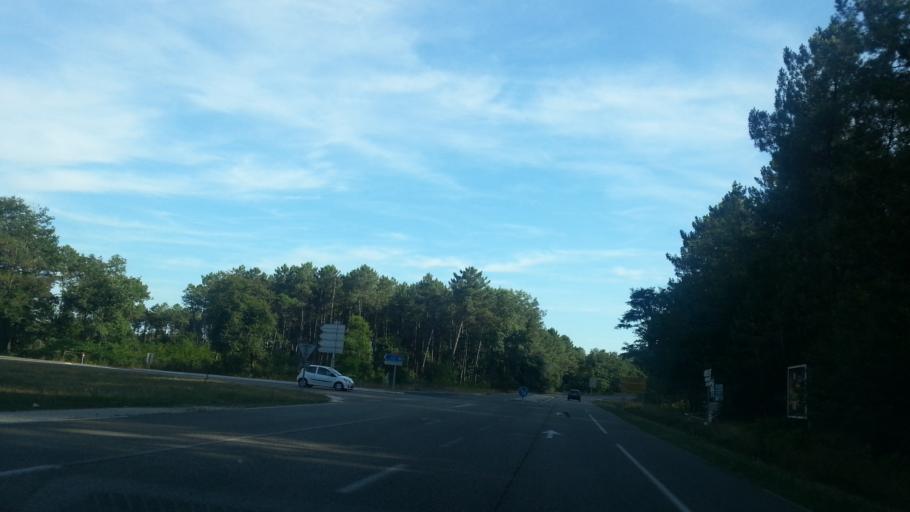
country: FR
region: Aquitaine
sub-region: Departement de la Gironde
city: Illats
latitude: 44.6126
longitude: -0.3723
